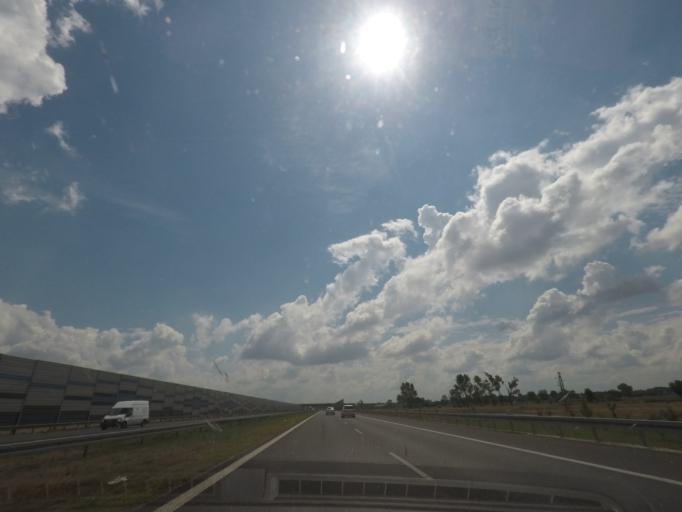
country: PL
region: Lodz Voivodeship
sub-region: Powiat zgierski
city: Strykow
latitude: 51.9618
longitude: 19.5892
